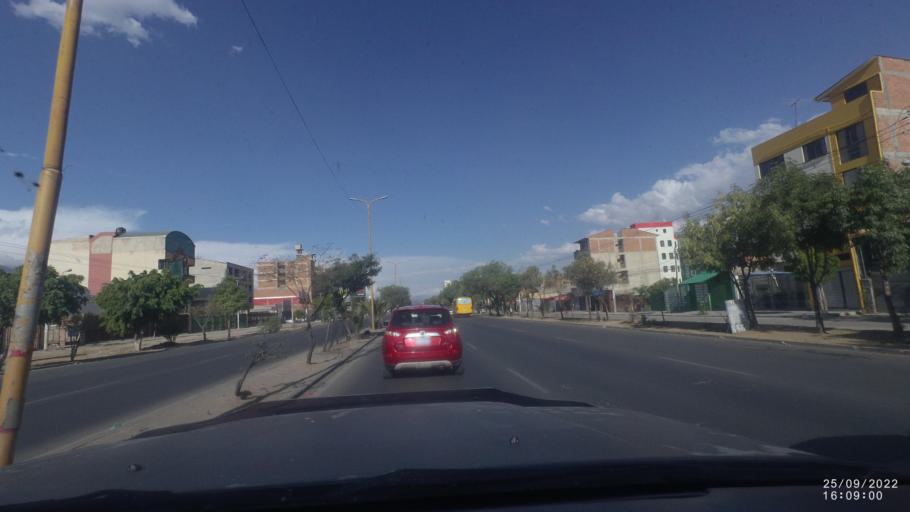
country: BO
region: Cochabamba
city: Cochabamba
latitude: -17.3929
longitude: -66.2114
